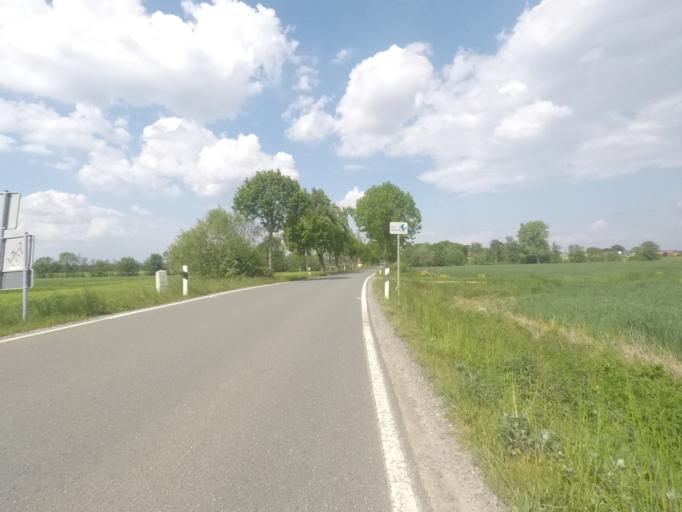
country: DE
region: North Rhine-Westphalia
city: Spenge
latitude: 52.1865
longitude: 8.5128
